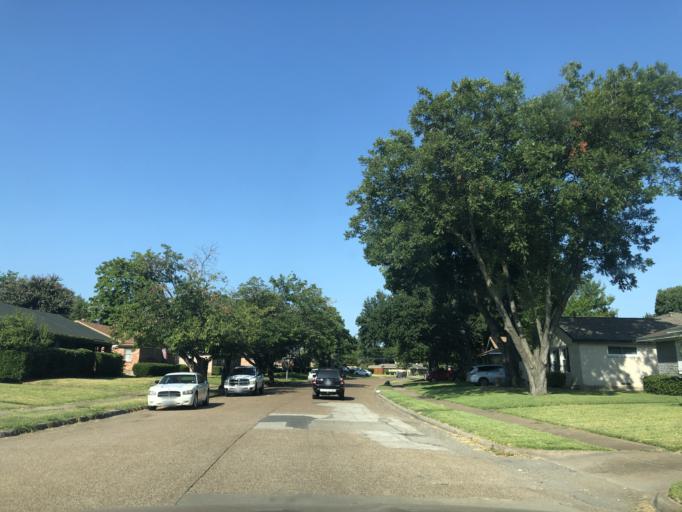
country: US
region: Texas
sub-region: Dallas County
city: Garland
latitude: 32.8669
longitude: -96.6464
